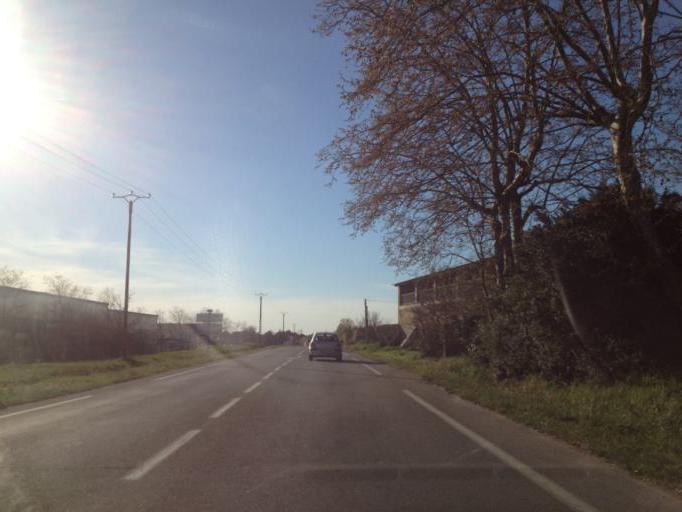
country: FR
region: Provence-Alpes-Cote d'Azur
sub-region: Departement des Bouches-du-Rhone
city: Saint-Cannat
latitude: 43.6145
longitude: 5.3199
